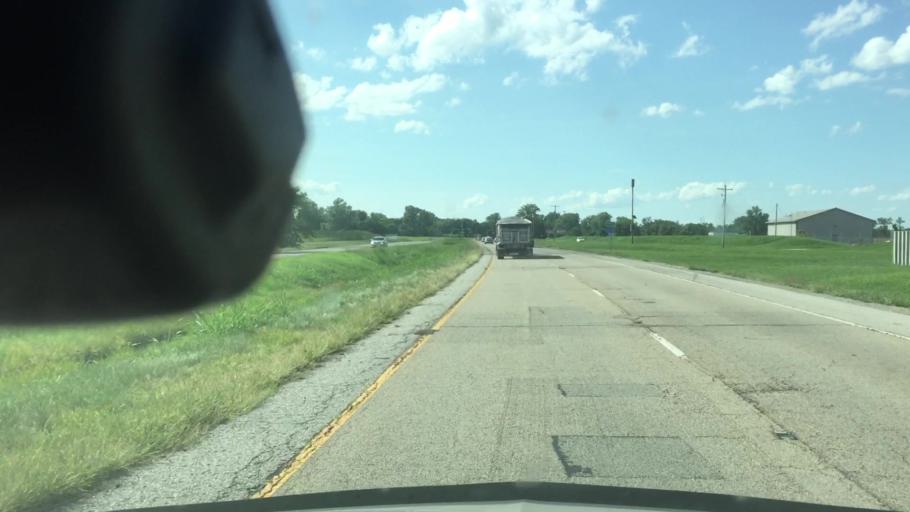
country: US
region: Illinois
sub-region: Madison County
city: Madison
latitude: 38.6597
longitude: -90.1372
